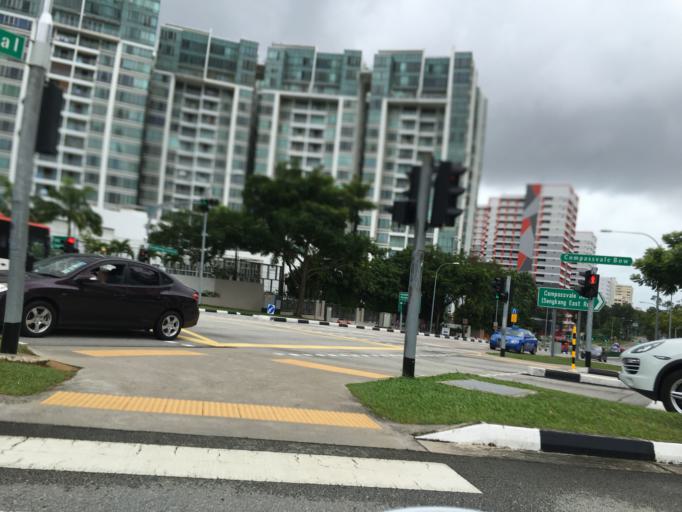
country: MY
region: Johor
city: Kampung Pasir Gudang Baru
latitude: 1.3816
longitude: 103.8928
